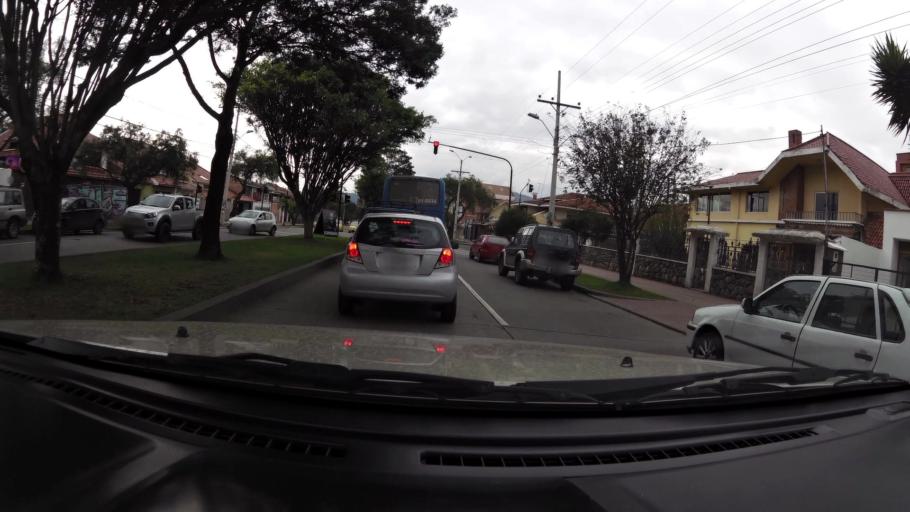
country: EC
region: Azuay
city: Cuenca
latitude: -2.9034
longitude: -79.0140
